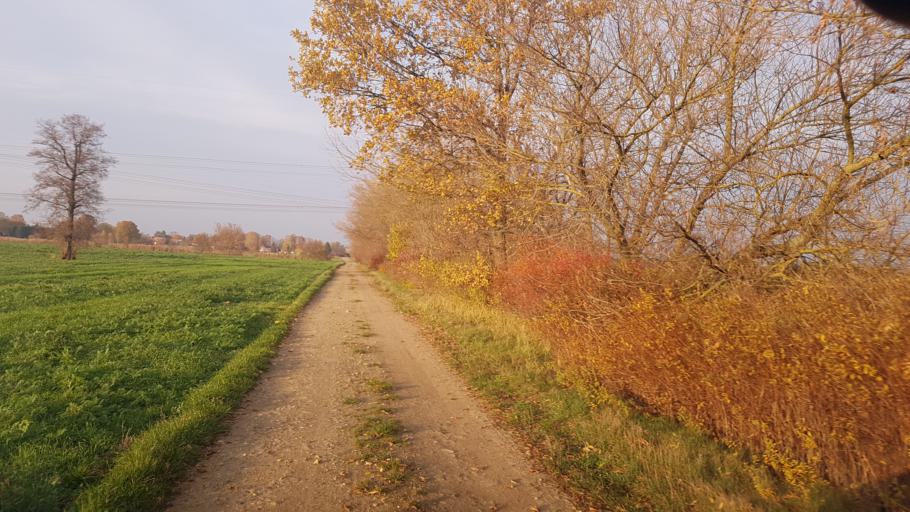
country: DE
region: Brandenburg
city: Schonewalde
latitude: 51.6515
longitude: 13.5990
